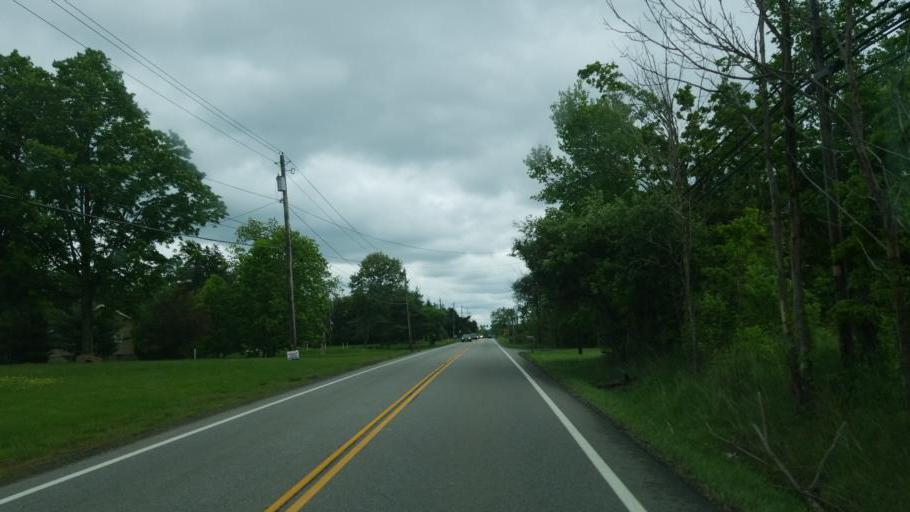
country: US
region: Ohio
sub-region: Medina County
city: Brunswick
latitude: 41.2384
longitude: -81.7687
